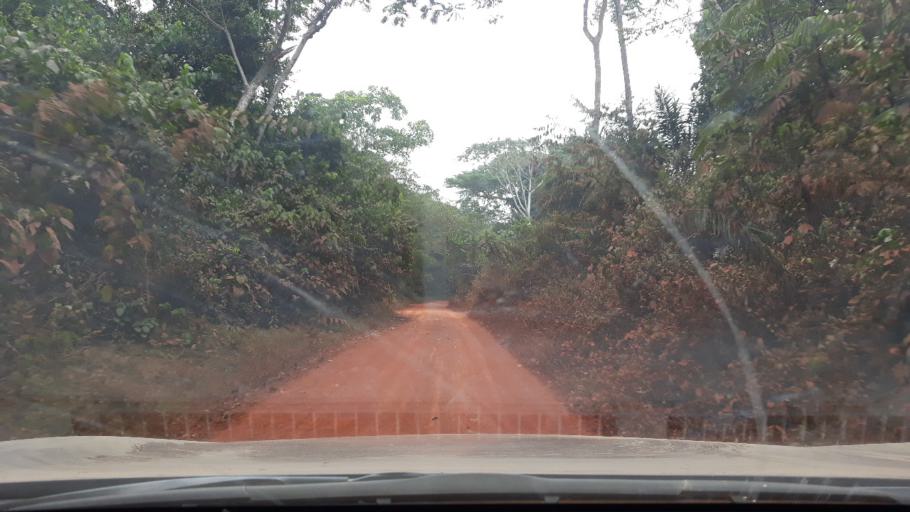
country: CD
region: Eastern Province
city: Buta
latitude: 2.2986
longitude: 25.0468
